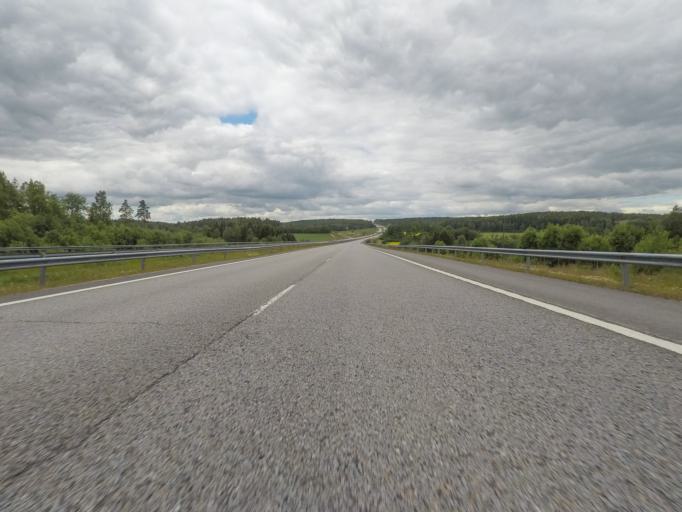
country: FI
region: Varsinais-Suomi
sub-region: Salo
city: Halikko
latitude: 60.4345
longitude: 22.9411
